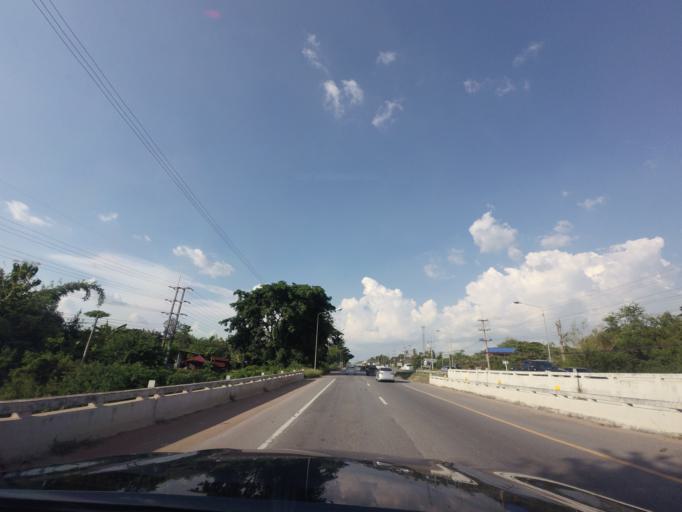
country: TH
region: Khon Kaen
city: Ban Phai
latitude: 16.0591
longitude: 102.7165
